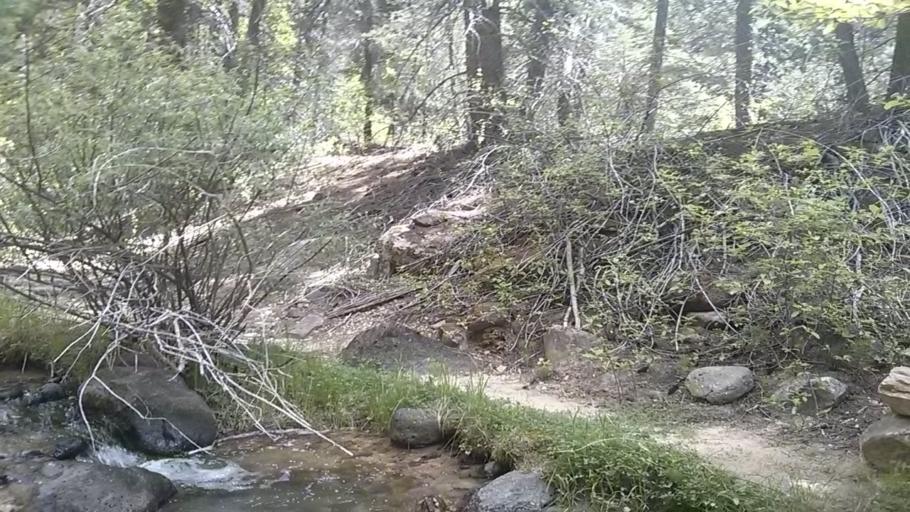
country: US
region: Utah
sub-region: Wayne County
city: Loa
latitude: 37.9573
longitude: -111.6507
